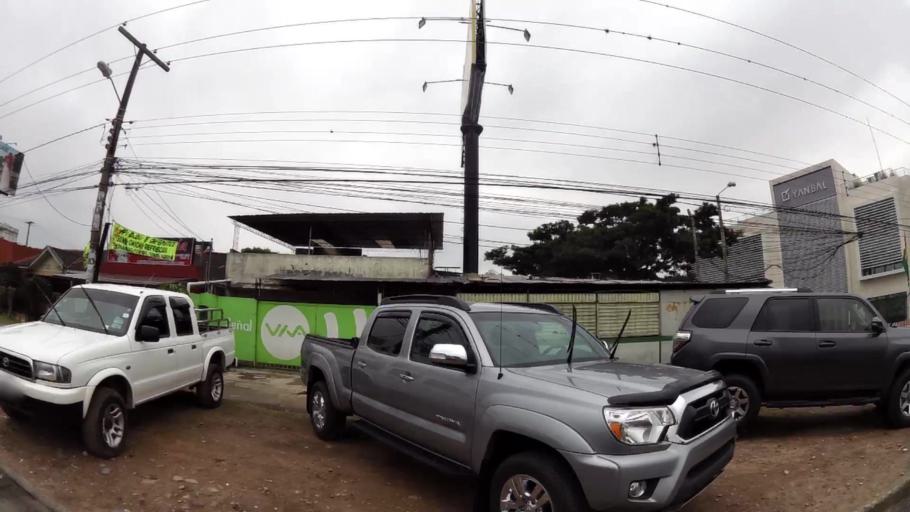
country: BO
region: Santa Cruz
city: Santa Cruz de la Sierra
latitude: -17.7704
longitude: -63.1817
